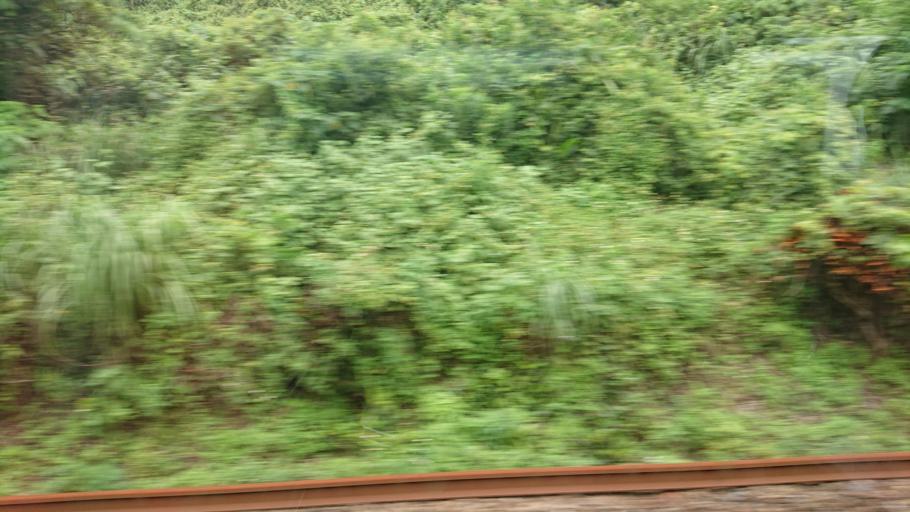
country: TW
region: Taiwan
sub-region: Yilan
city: Yilan
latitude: 24.9130
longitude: 121.8775
